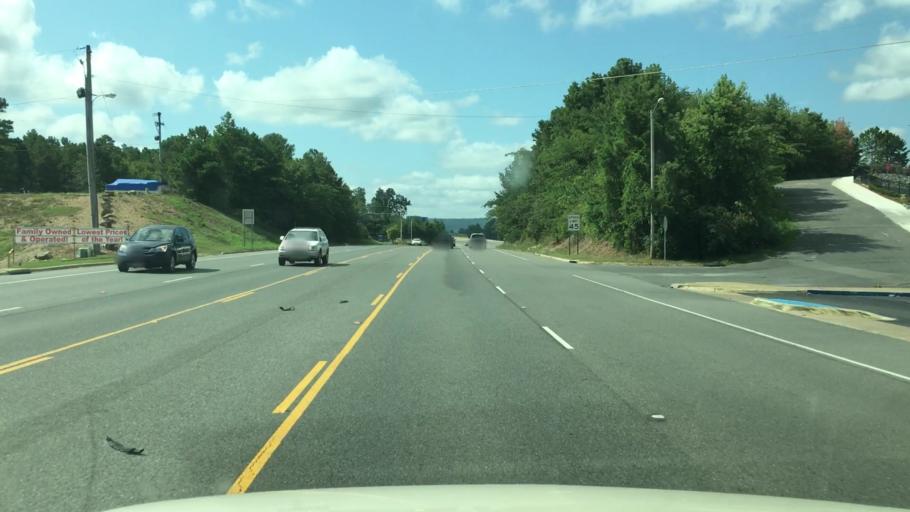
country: US
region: Arkansas
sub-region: Garland County
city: Lake Hamilton
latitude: 34.4388
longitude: -93.0884
